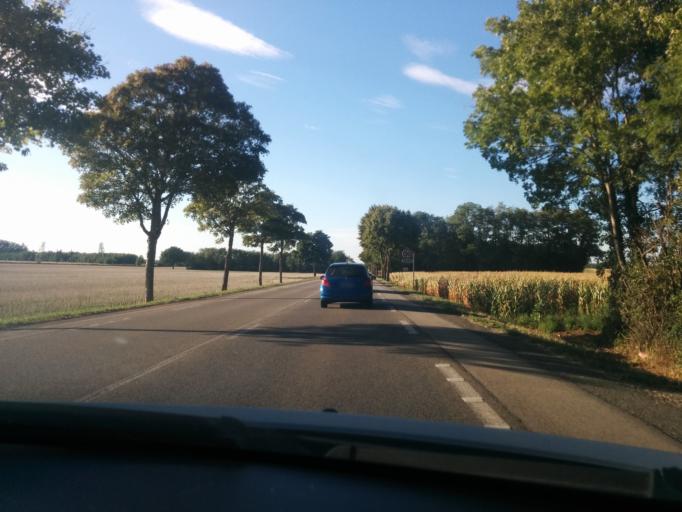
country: FR
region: Rhone-Alpes
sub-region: Departement de l'Ain
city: Tossiat
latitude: 46.1259
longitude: 5.2934
